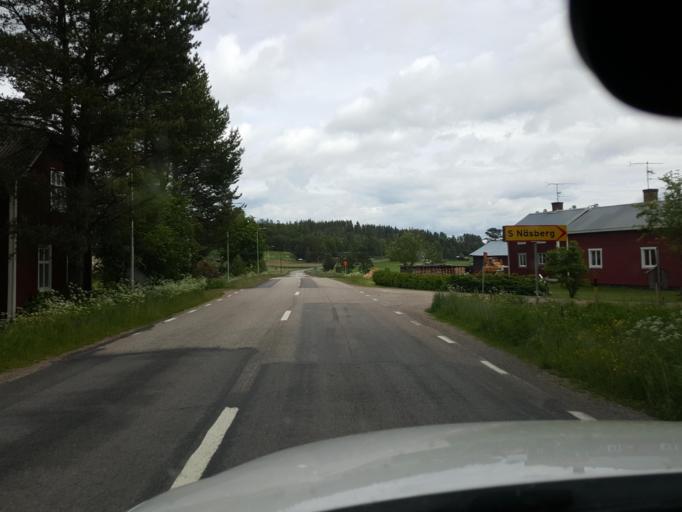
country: SE
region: Gaevleborg
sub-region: Ljusdals Kommun
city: Farila
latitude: 61.7946
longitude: 15.6487
